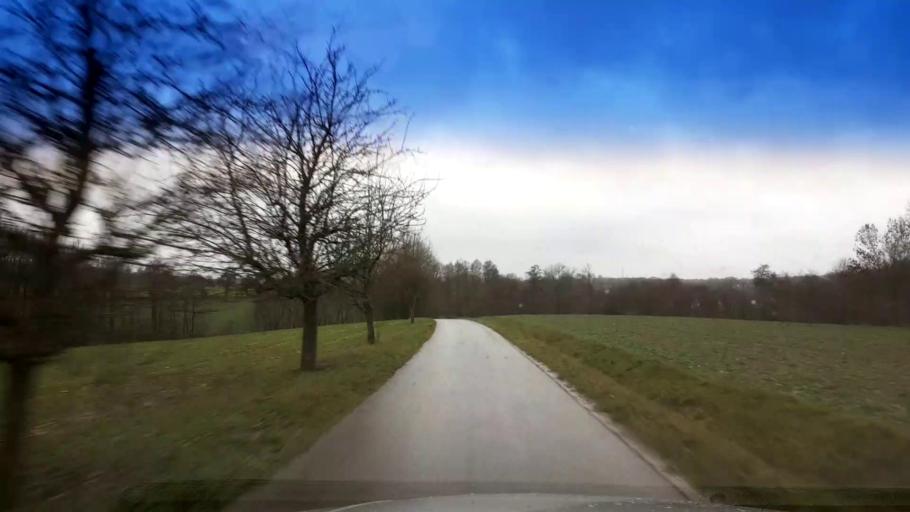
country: DE
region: Bavaria
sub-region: Upper Franconia
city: Litzendorf
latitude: 49.8691
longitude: 11.0375
